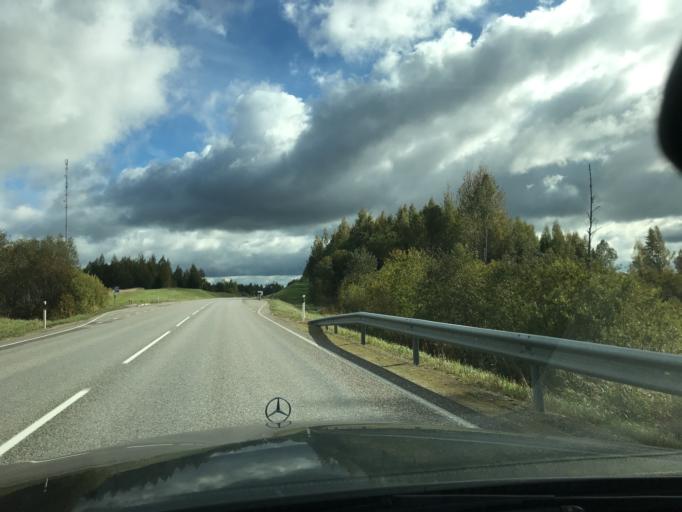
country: EE
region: Vorumaa
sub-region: Voru linn
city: Voru
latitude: 57.7494
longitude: 27.2386
